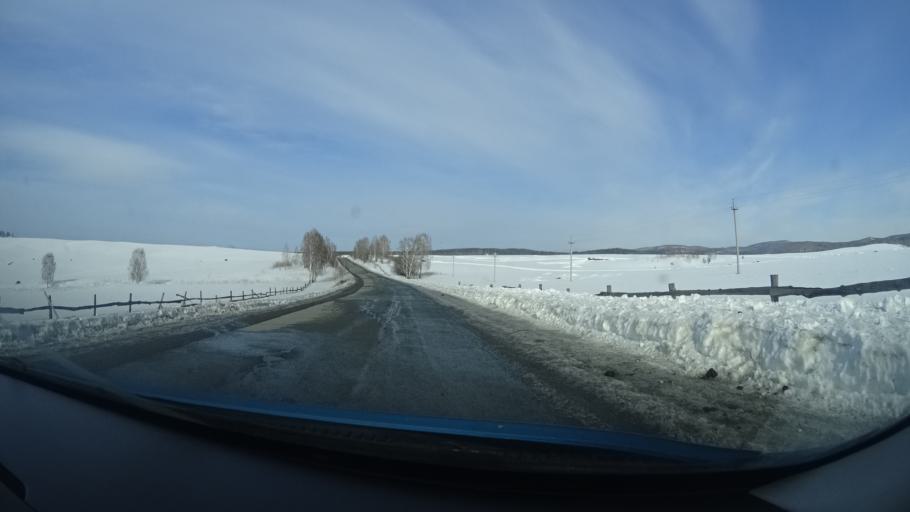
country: RU
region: Bashkortostan
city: Lomovka
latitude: 53.8063
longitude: 58.2716
